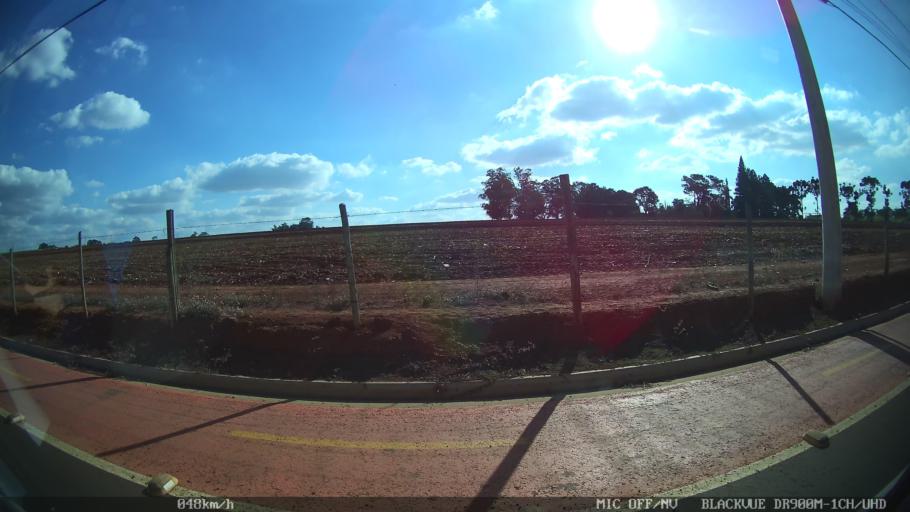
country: BR
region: Sao Paulo
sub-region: Nova Odessa
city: Nova Odessa
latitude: -22.8123
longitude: -47.3216
